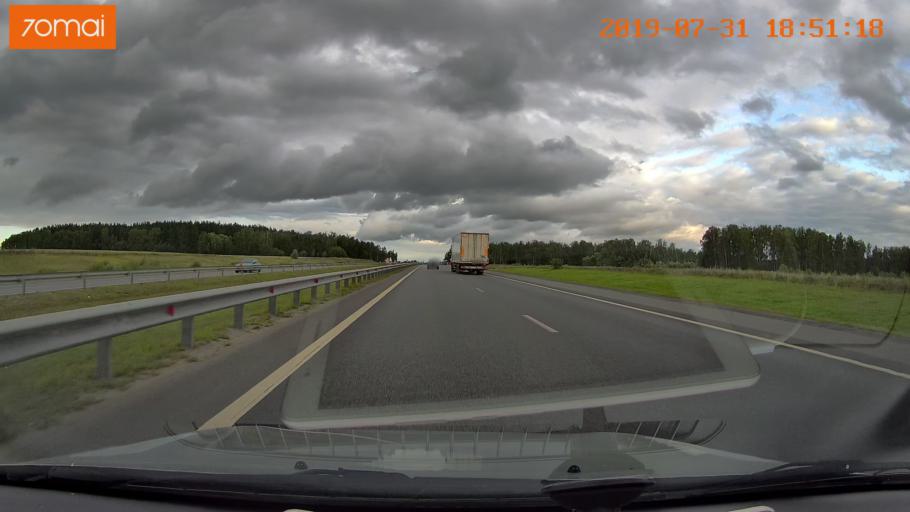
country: RU
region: Moskovskaya
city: Troitskoye
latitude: 55.2225
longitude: 38.6034
